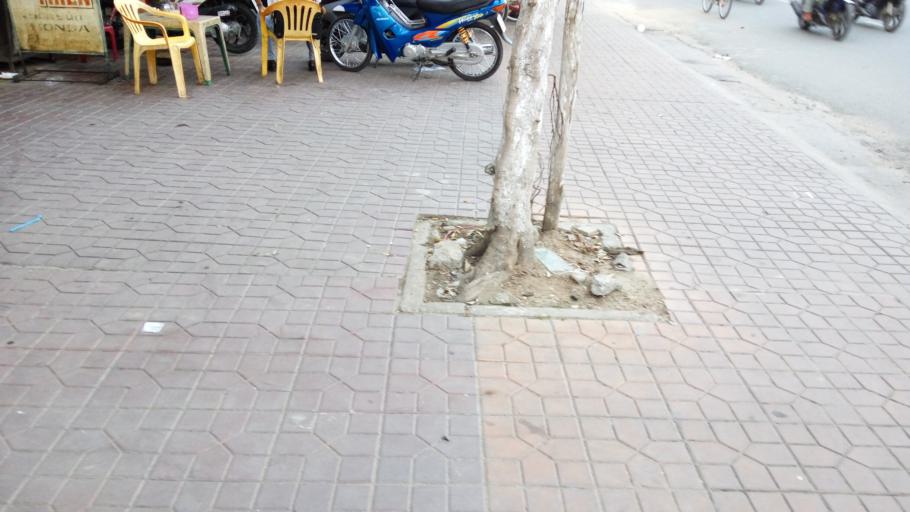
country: VN
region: An Giang
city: Long Xuyen
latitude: 10.3796
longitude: 105.4392
